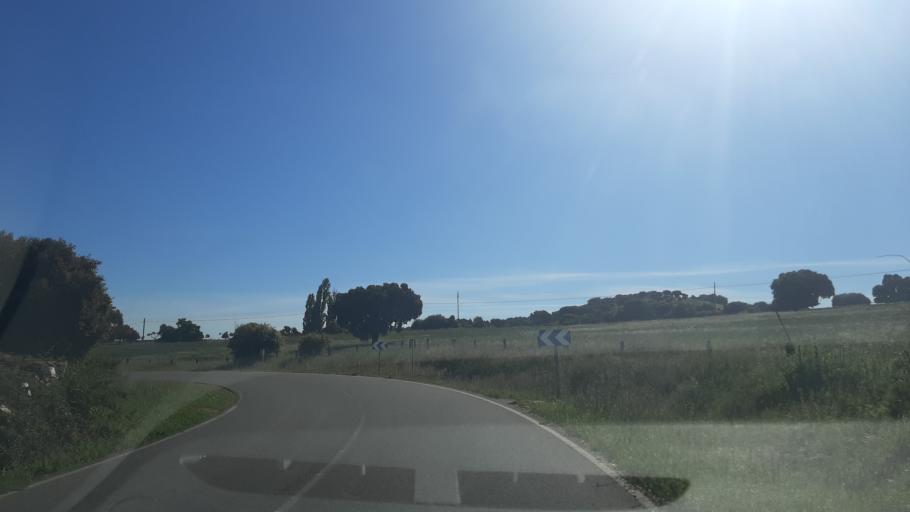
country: ES
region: Castille and Leon
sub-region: Provincia de Salamanca
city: Salvatierra de Tormes
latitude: 40.5569
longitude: -5.5837
